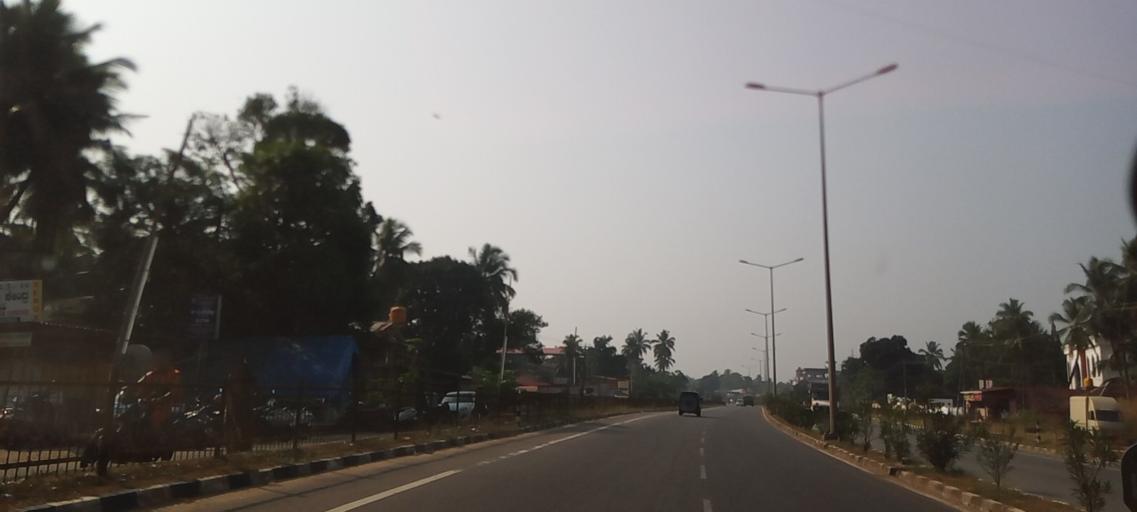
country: IN
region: Karnataka
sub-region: Udupi
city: Coondapoor
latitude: 13.5243
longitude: 74.7059
